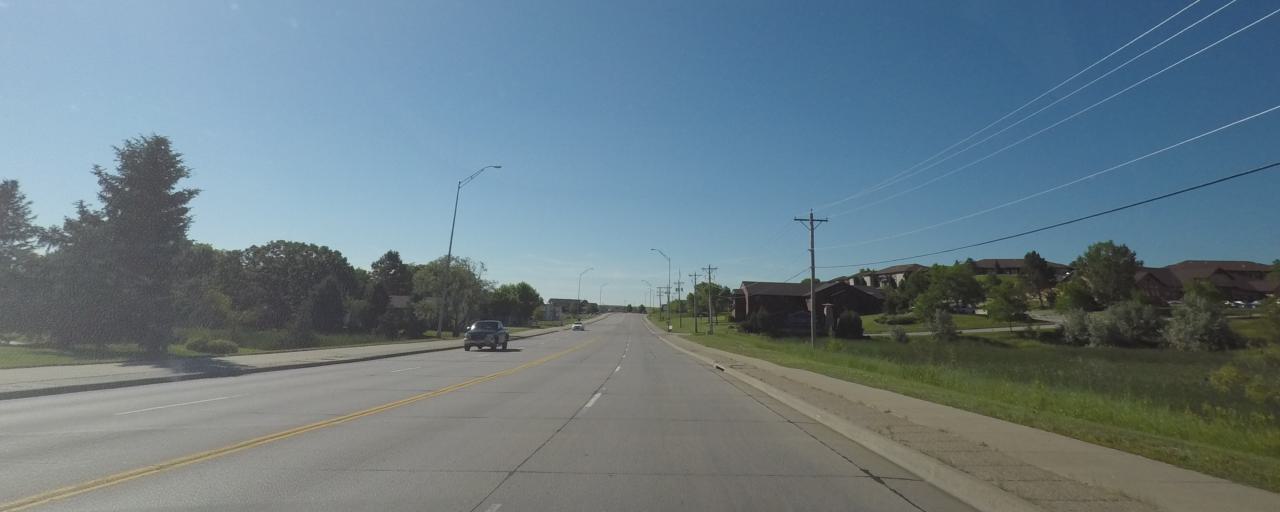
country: US
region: South Dakota
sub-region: Pennington County
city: Rapid City
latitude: 44.0476
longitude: -103.2226
